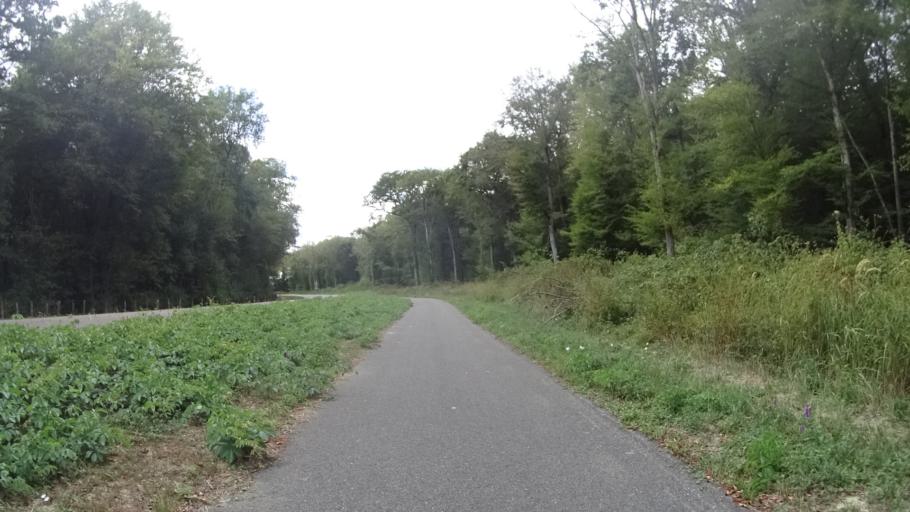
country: FR
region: Franche-Comte
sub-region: Departement du Jura
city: Damparis
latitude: 47.0744
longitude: 5.3735
